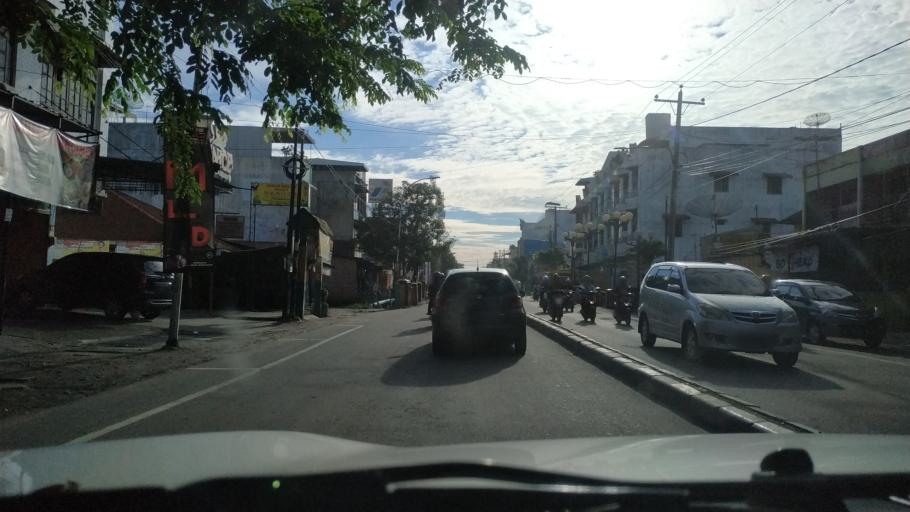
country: ID
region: North Sumatra
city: Medan
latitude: 3.5985
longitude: 98.6947
